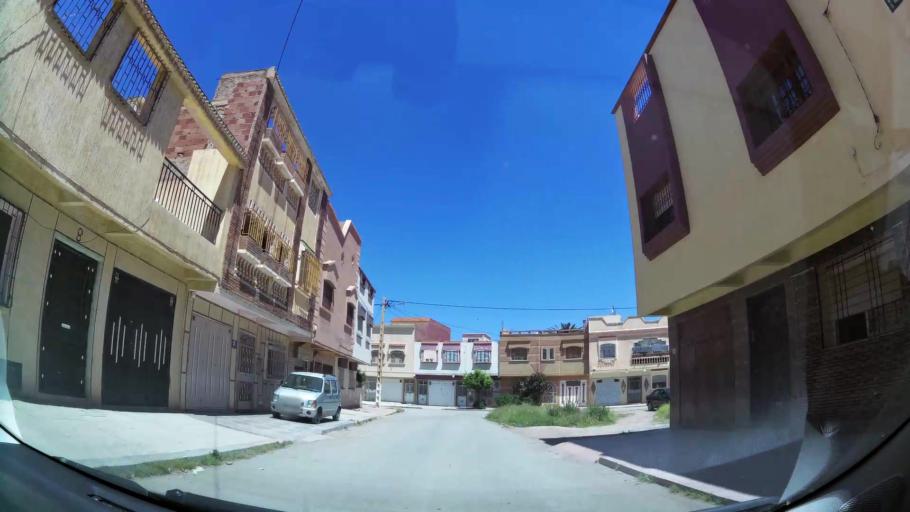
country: MA
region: Oriental
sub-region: Oujda-Angad
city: Oujda
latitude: 34.6658
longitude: -1.8945
